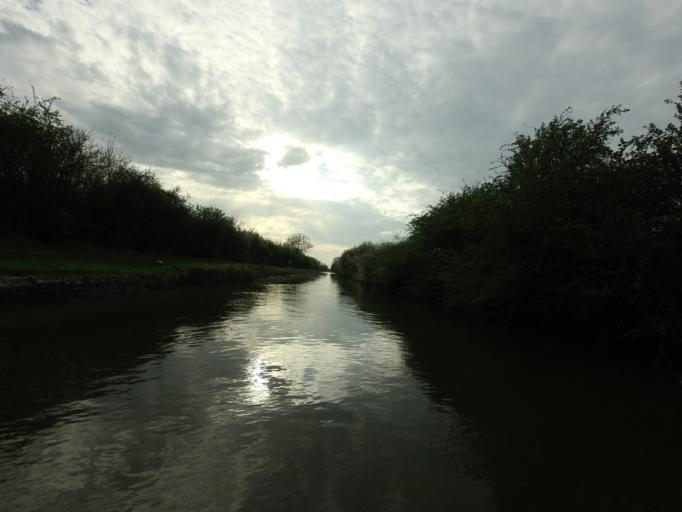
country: GB
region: England
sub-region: Buckinghamshire
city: Aston Clinton
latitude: 51.8171
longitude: -0.7290
